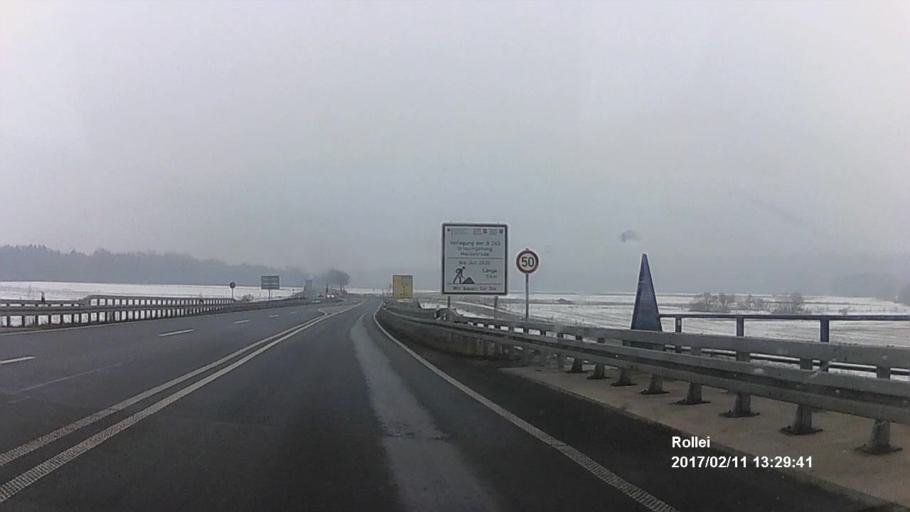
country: DE
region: Lower Saxony
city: Bad Sachsa
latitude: 51.5778
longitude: 10.5151
